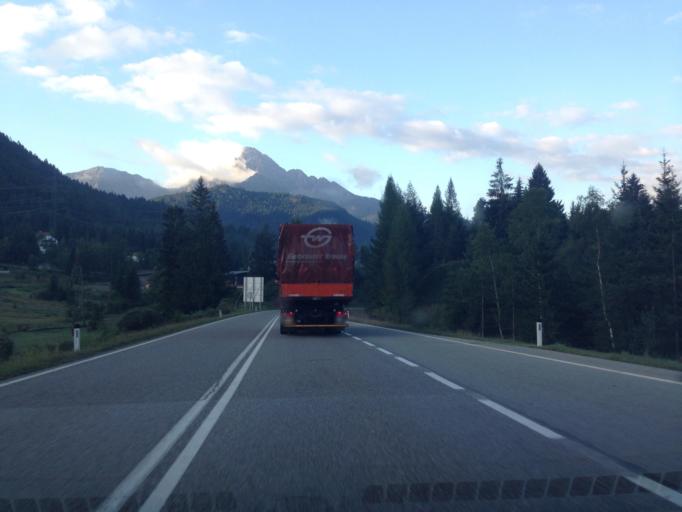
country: AT
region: Tyrol
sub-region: Politischer Bezirk Reutte
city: Breitenwang
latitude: 47.4879
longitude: 10.7434
